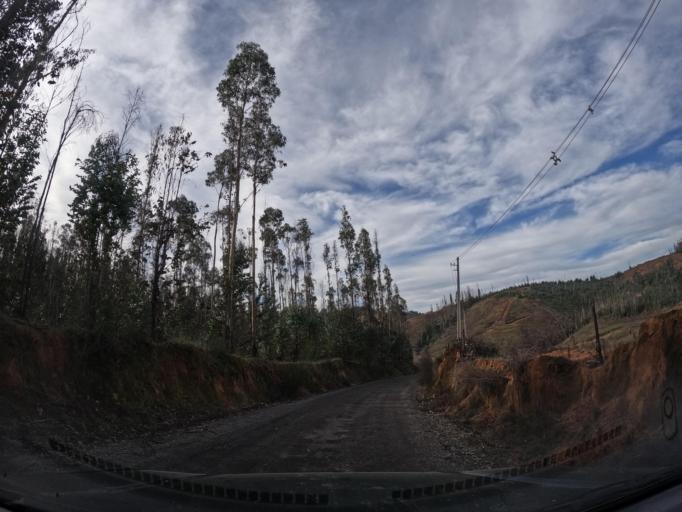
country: CL
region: Biobio
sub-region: Provincia de Concepcion
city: Chiguayante
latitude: -37.0189
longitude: -72.9089
